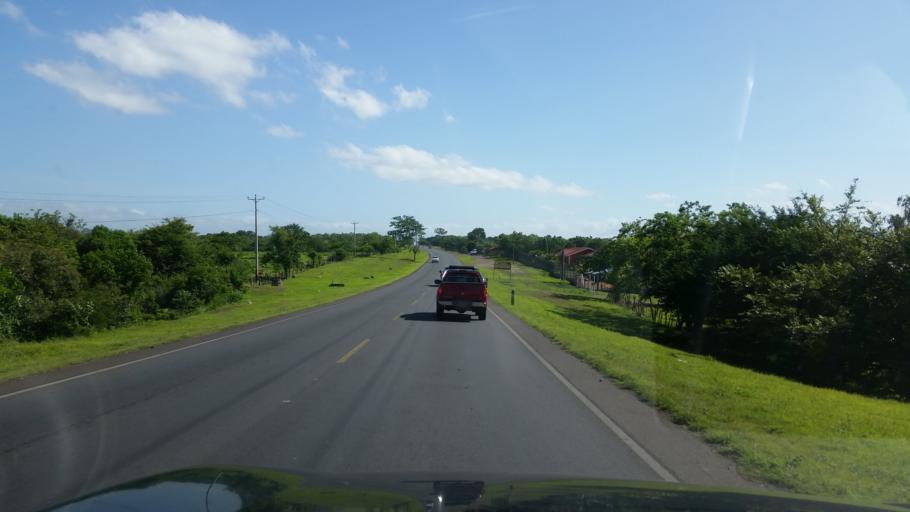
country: NI
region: Matagalpa
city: Ciudad Dario
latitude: 12.7594
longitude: -86.1249
